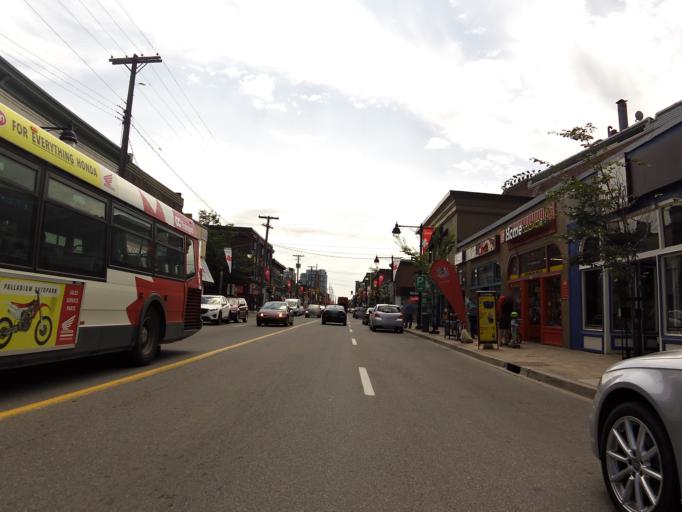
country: CA
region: Ontario
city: Ottawa
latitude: 45.4041
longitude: -75.6891
